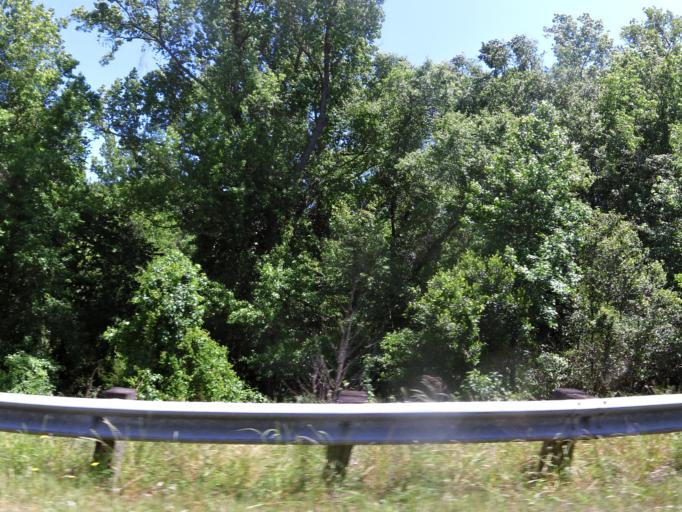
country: US
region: South Carolina
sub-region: Aiken County
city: Clearwater
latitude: 33.4952
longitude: -81.9140
